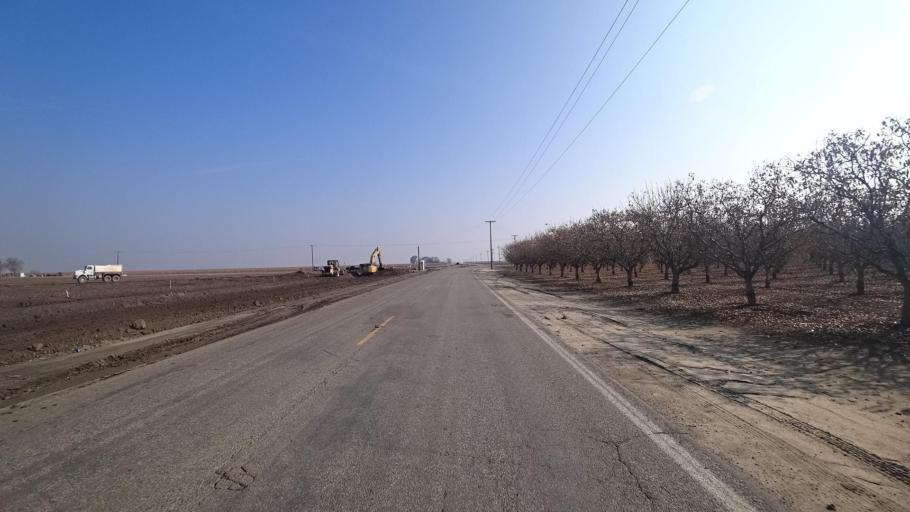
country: US
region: California
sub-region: Kern County
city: Buttonwillow
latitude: 35.3546
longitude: -119.4139
